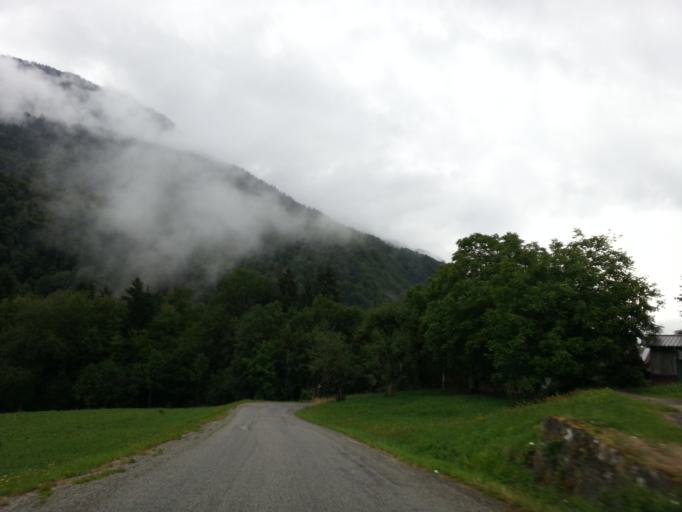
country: FR
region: Rhone-Alpes
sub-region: Departement de la Savoie
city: Marthod
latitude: 45.7130
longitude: 6.4763
